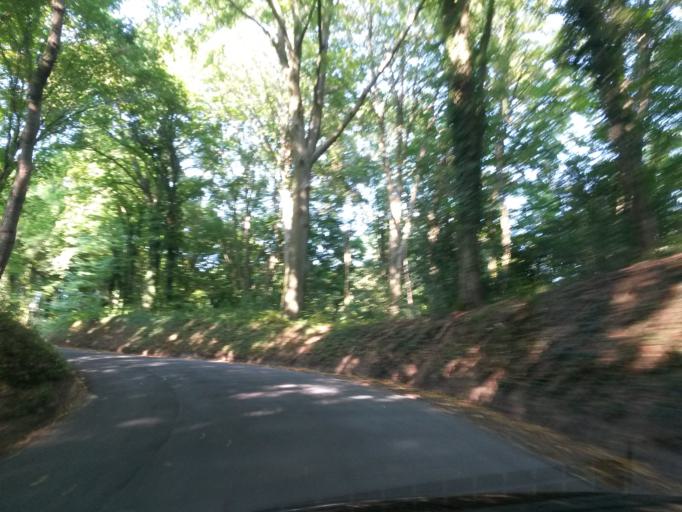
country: DE
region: North Rhine-Westphalia
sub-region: Regierungsbezirk Koln
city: Rosrath
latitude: 50.8768
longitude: 7.2088
